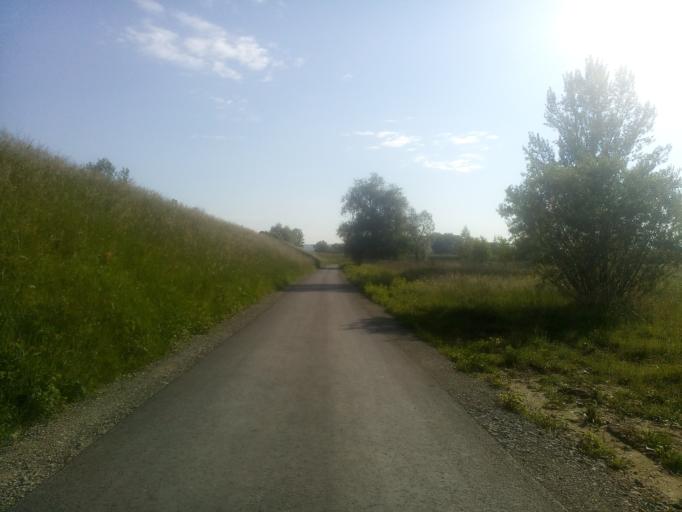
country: PL
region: Lesser Poland Voivodeship
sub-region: Powiat nowosadecki
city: Chelmiec
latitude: 49.6083
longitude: 20.6751
